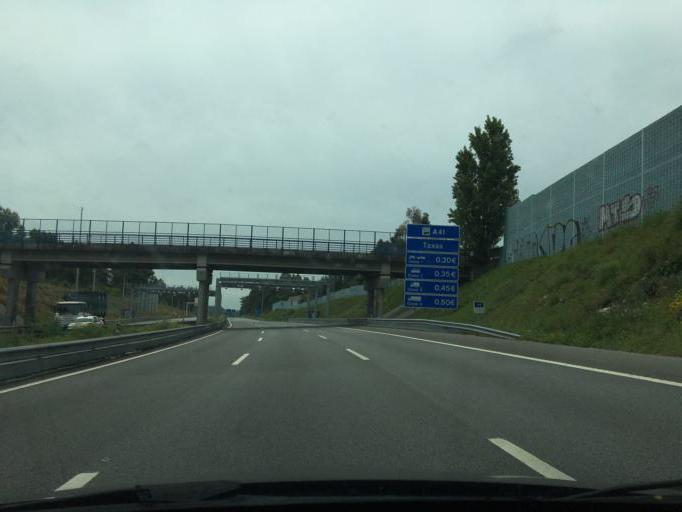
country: PT
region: Porto
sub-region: Matosinhos
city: Santa Cruz do Bispo
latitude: 41.2318
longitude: -8.6831
